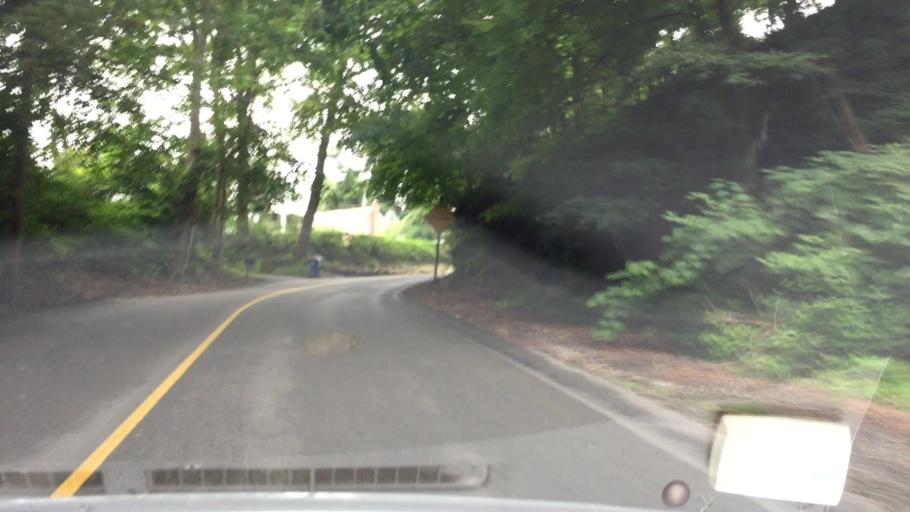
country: US
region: Pennsylvania
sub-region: Allegheny County
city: Millvale
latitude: 40.5031
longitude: -79.9822
